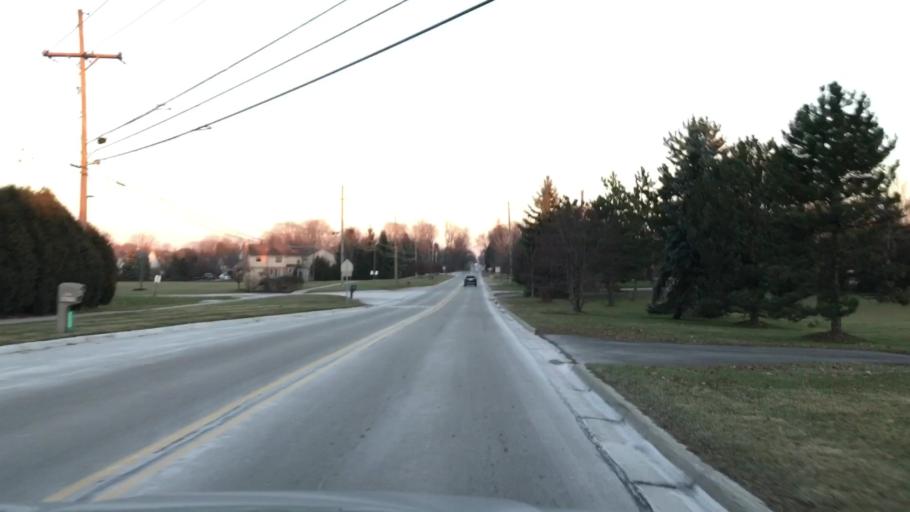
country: US
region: Michigan
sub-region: Wayne County
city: Northville
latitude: 42.4511
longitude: -83.5067
